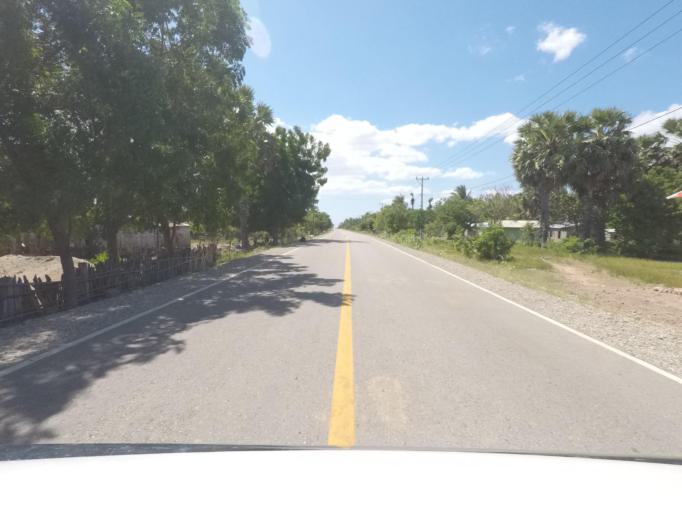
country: TL
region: Lautem
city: Lospalos
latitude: -8.3767
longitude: 126.8709
